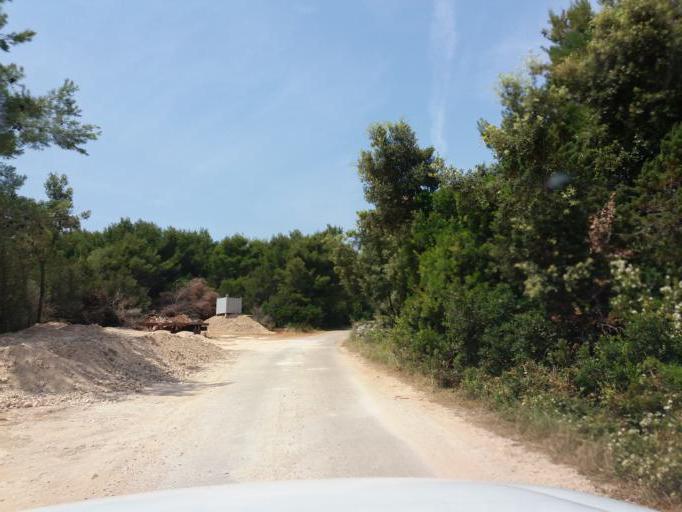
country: HR
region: Zadarska
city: Ugljan
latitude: 44.1424
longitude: 14.8436
